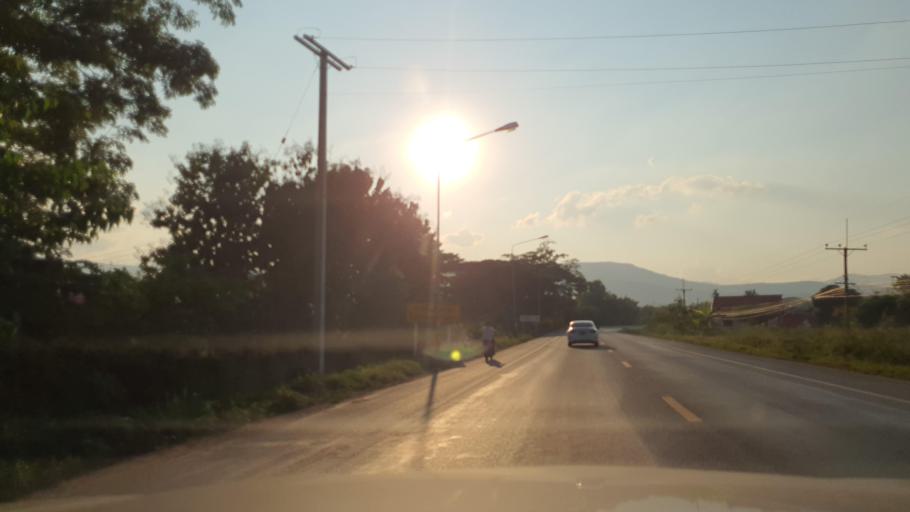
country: TH
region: Phayao
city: Phayao
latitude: 19.0801
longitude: 99.8698
